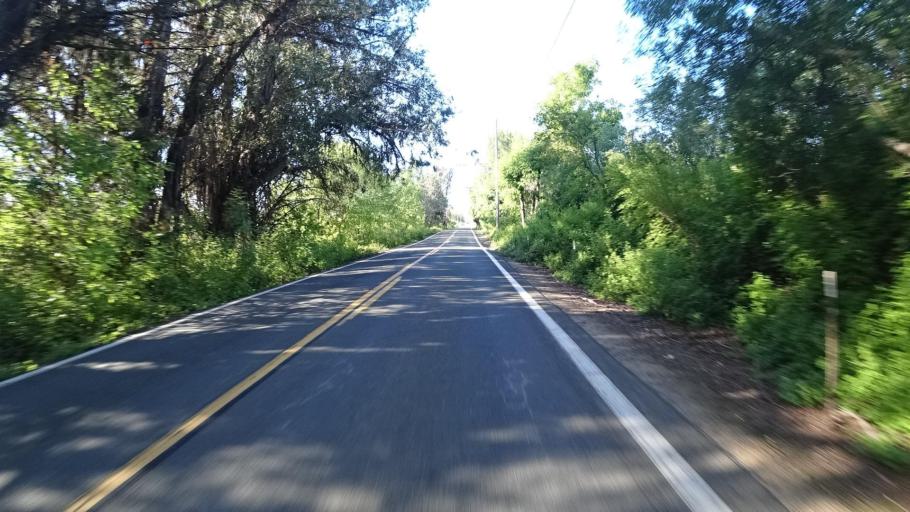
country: US
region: California
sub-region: Lake County
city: North Lakeport
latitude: 39.0878
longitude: -122.9499
